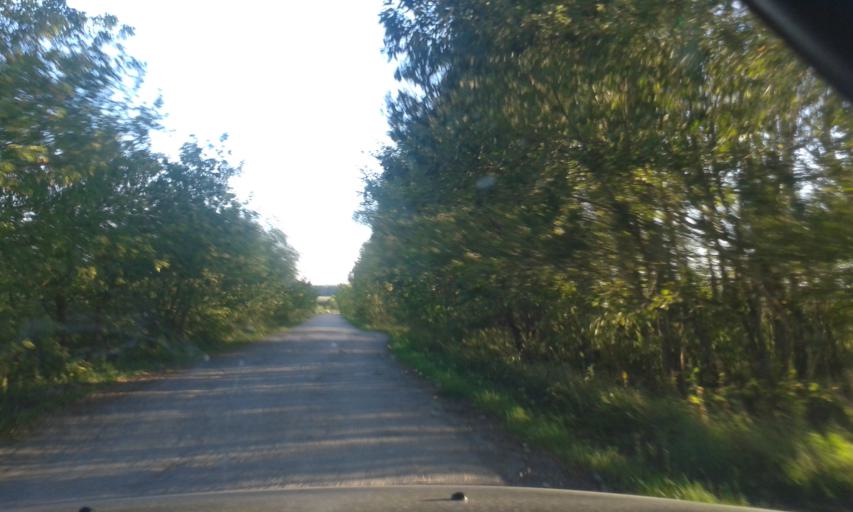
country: RU
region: Tula
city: Krapivna
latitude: 54.1269
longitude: 37.1555
